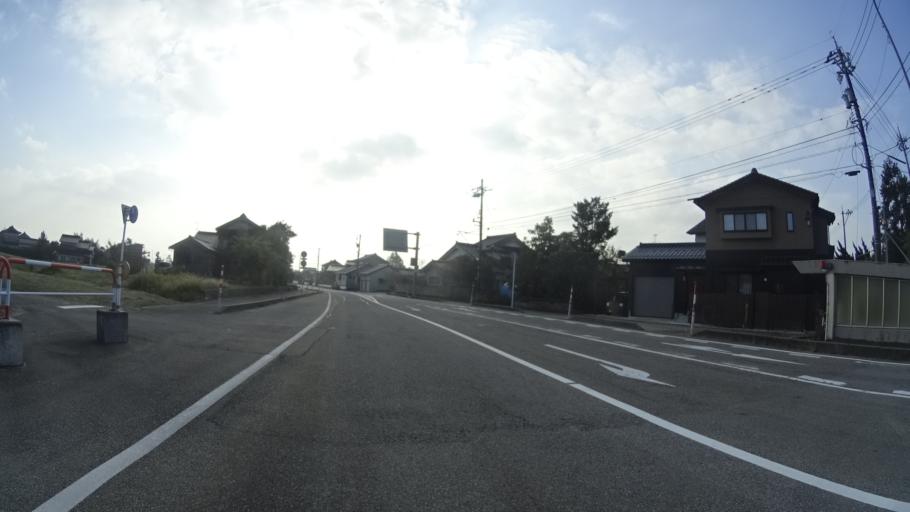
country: JP
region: Toyama
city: Himi
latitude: 36.8762
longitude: 136.9756
